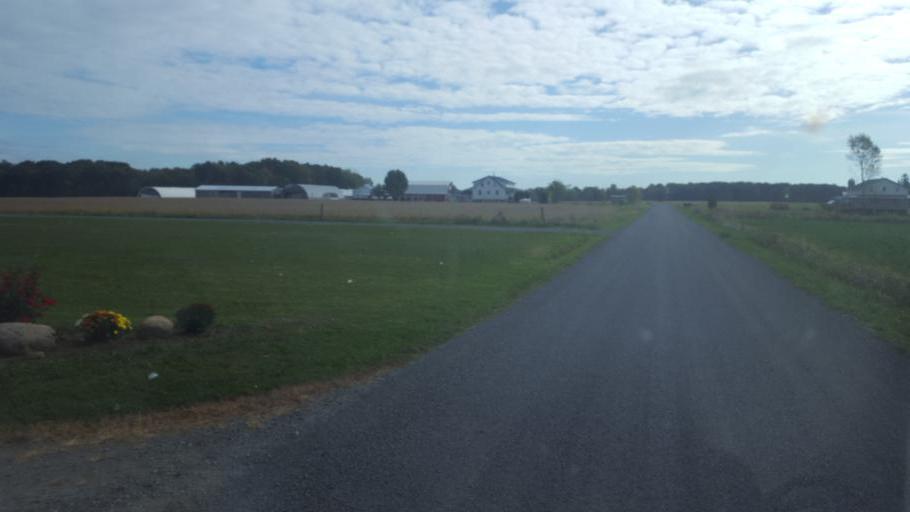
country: US
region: Pennsylvania
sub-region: Mercer County
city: Reynolds Heights
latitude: 41.3326
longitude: -80.3170
